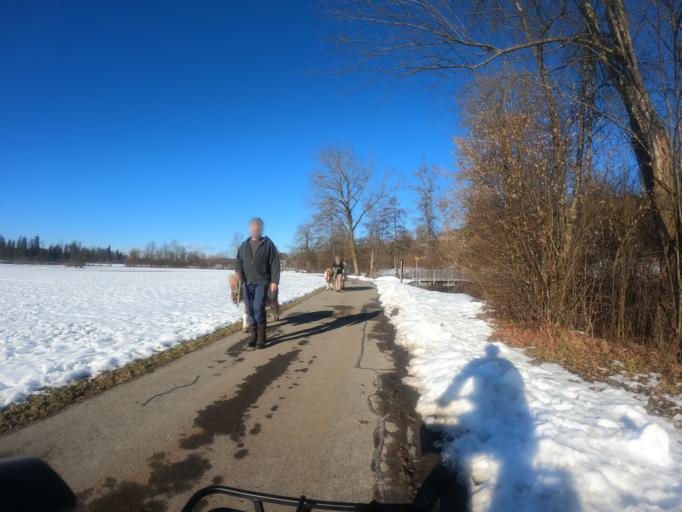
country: CH
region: Aargau
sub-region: Bezirk Bremgarten
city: Oberlunkhofen
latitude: 47.3104
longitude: 8.3855
